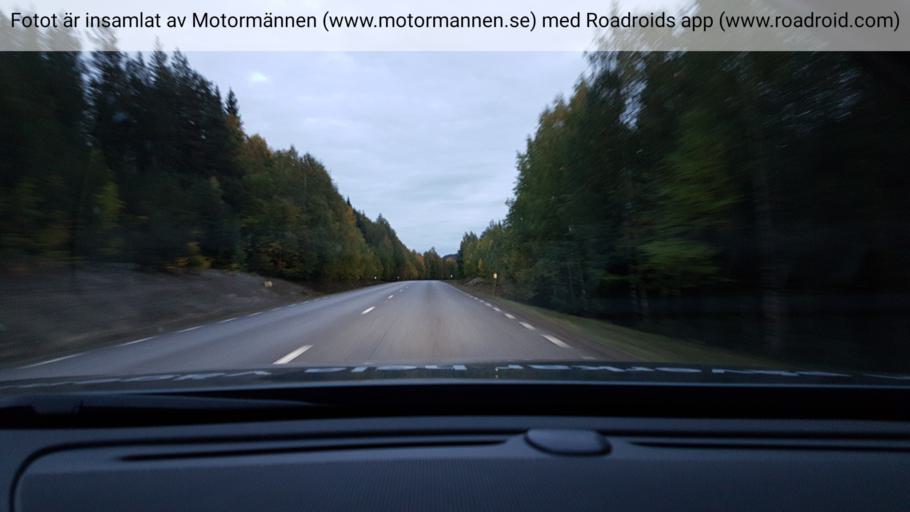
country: SE
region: Norrbotten
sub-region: Alvsbyns Kommun
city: AElvsbyn
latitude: 65.8028
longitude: 20.6282
